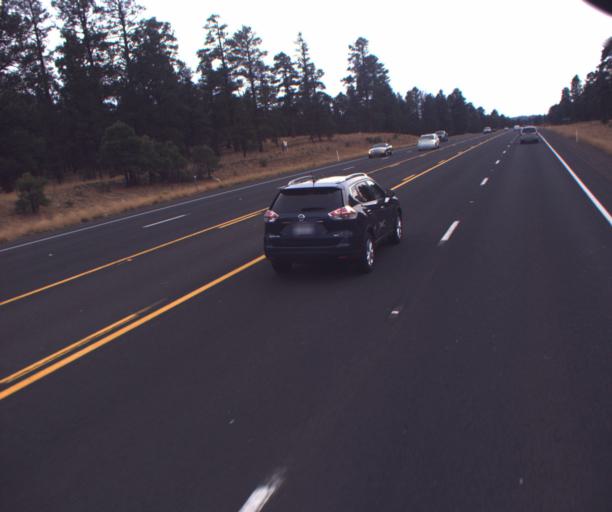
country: US
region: Arizona
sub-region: Coconino County
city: Flagstaff
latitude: 35.2808
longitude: -111.5426
